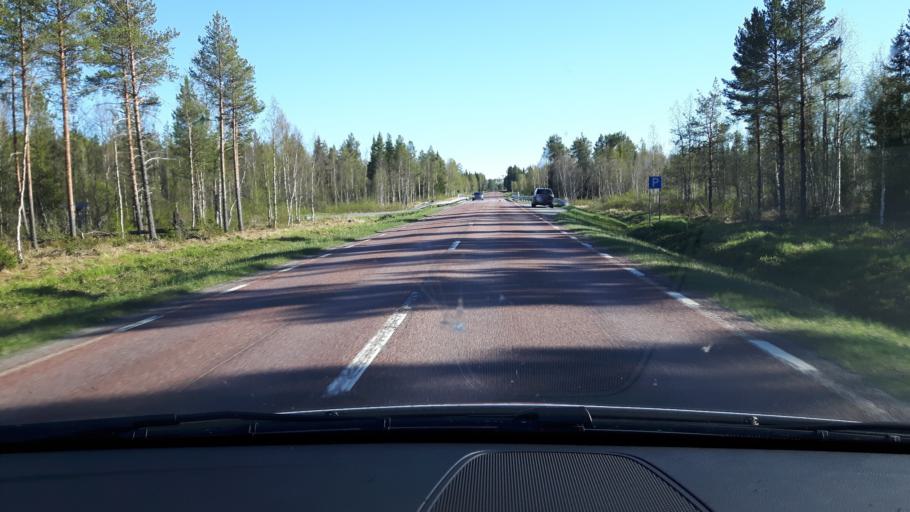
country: SE
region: Jaemtland
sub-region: Stroemsunds Kommun
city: Stroemsund
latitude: 63.7584
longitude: 15.4995
